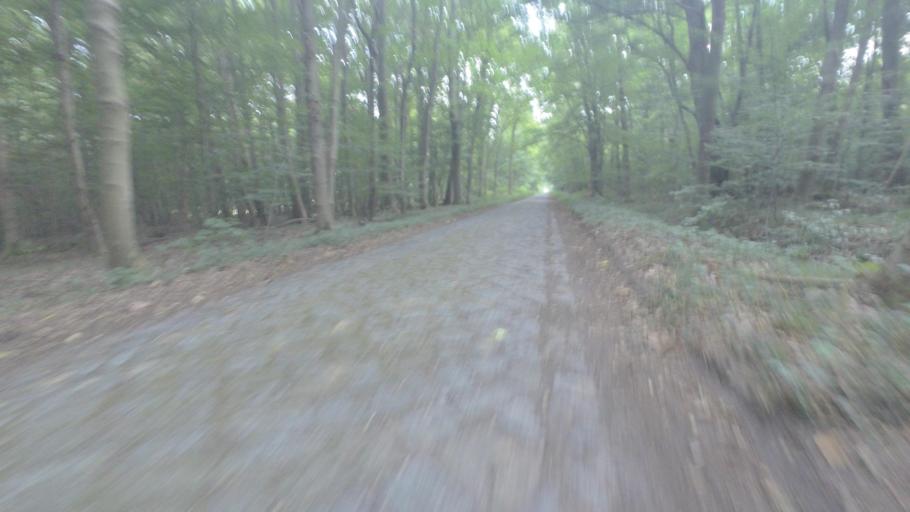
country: DE
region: Brandenburg
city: Wittstock
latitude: 53.2500
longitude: 12.4717
